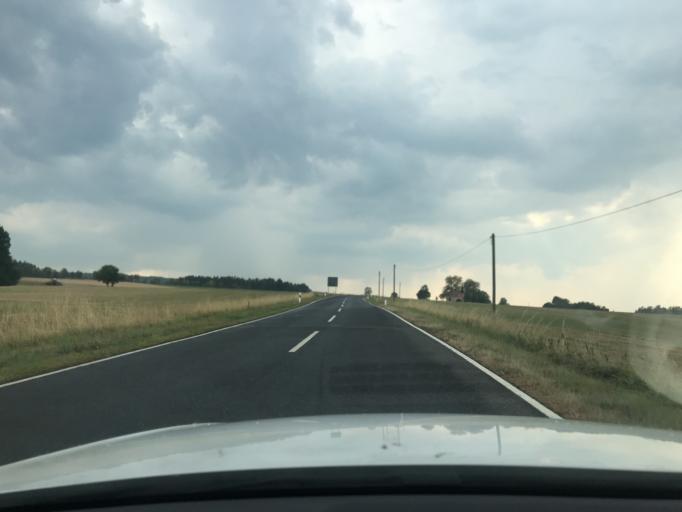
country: DE
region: Bavaria
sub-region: Upper Palatinate
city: Schlammersdorf
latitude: 49.8014
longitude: 11.7276
